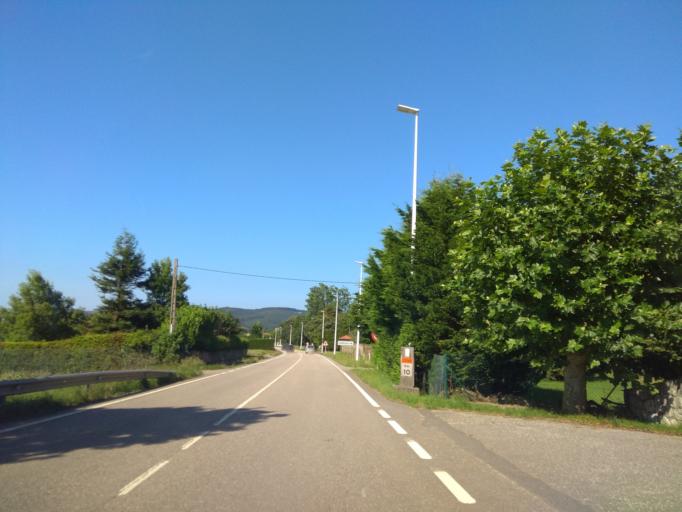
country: ES
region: Cantabria
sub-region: Provincia de Cantabria
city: Entrambasaguas
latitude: 43.4528
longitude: -3.6787
